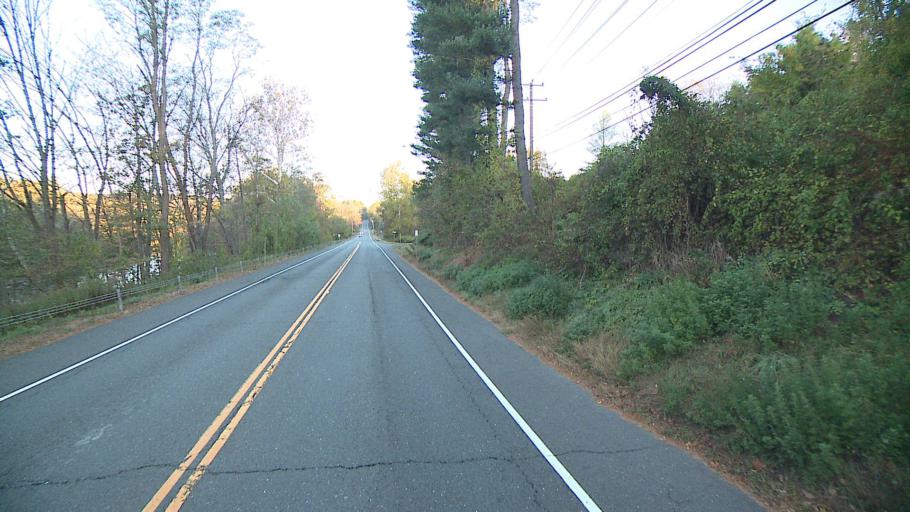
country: US
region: Connecticut
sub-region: Hartford County
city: Collinsville
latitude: 41.8420
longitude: -72.9378
